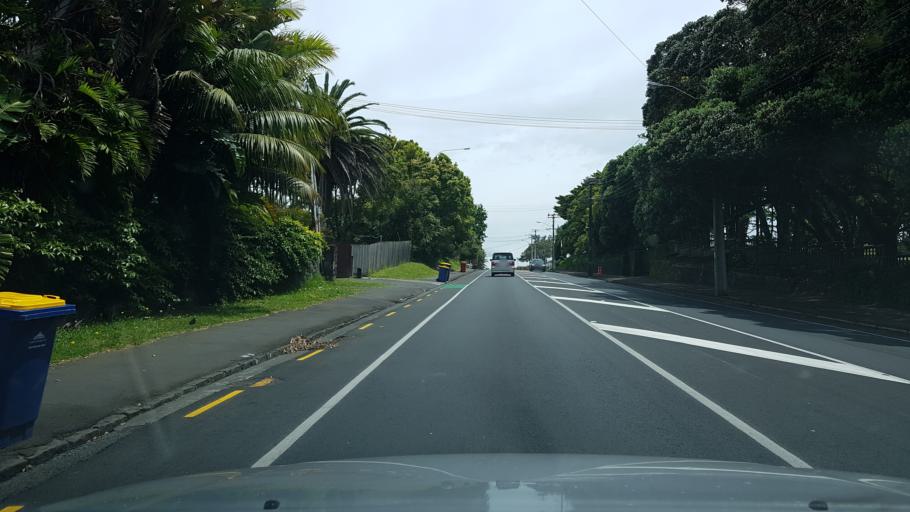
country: NZ
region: Auckland
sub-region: Auckland
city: North Shore
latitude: -36.8000
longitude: 174.7863
